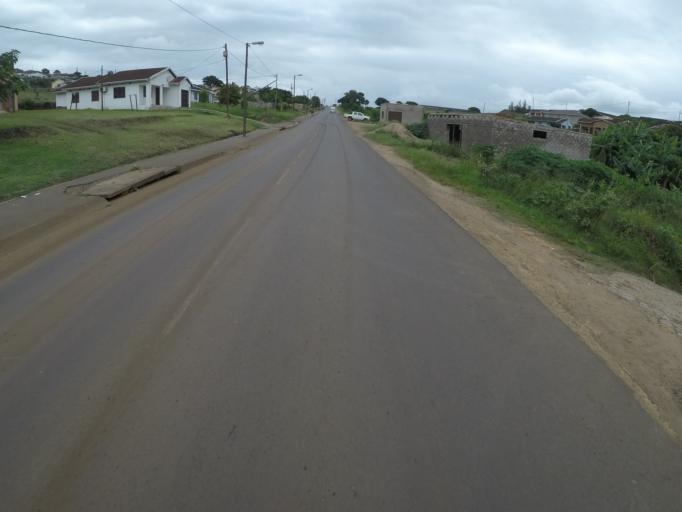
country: ZA
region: KwaZulu-Natal
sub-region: uThungulu District Municipality
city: Empangeni
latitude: -28.7829
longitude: 31.8600
